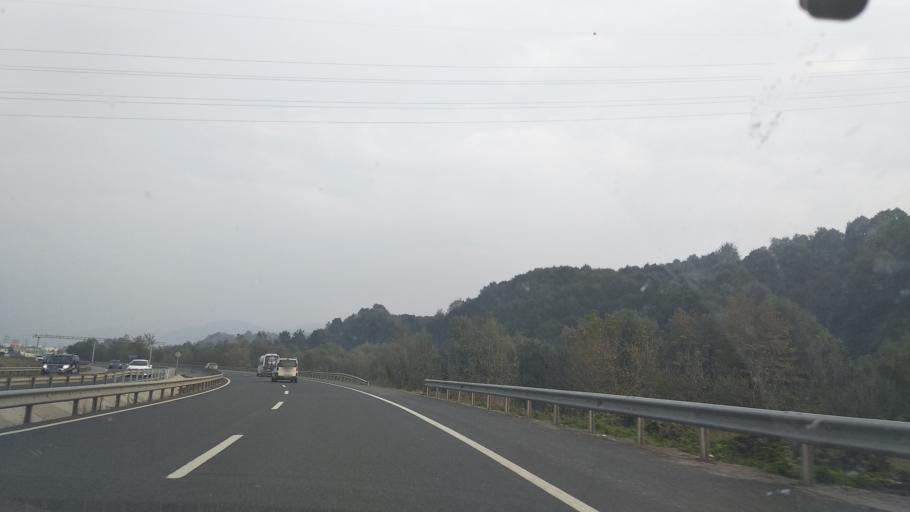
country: TR
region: Duzce
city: Kaynasli
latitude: 40.7847
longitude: 31.2674
